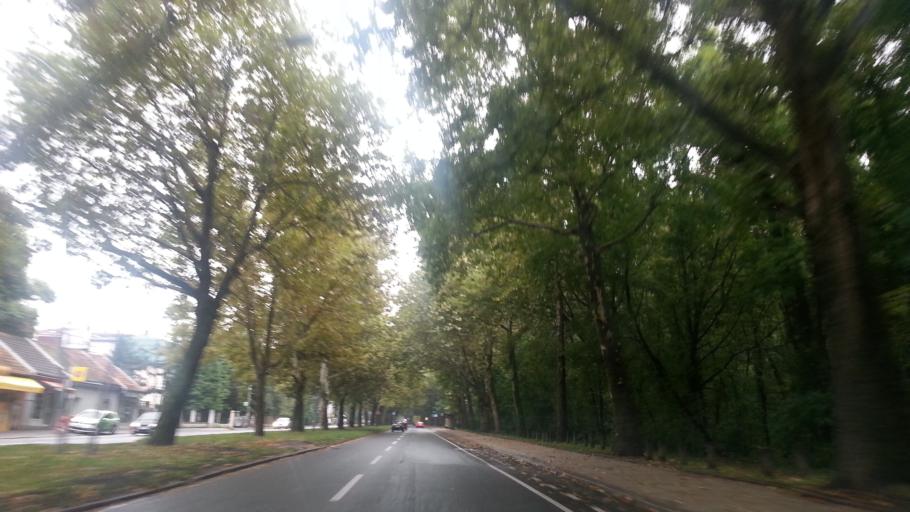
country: RS
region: Central Serbia
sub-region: Belgrade
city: Vozdovac
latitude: 44.7666
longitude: 20.4776
